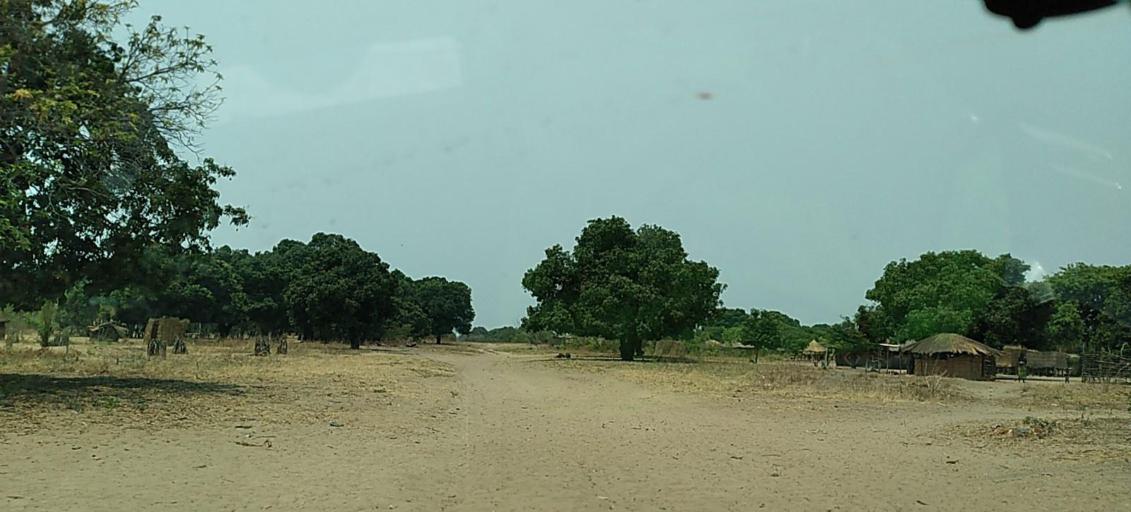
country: ZM
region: Western
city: Lukulu
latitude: -14.1556
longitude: 23.3054
